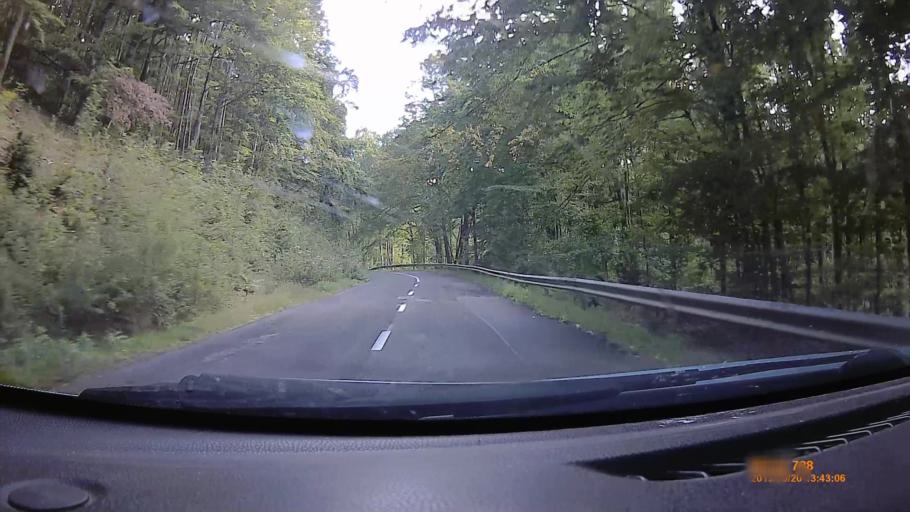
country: HU
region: Heves
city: Szilvasvarad
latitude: 48.0598
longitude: 20.5505
